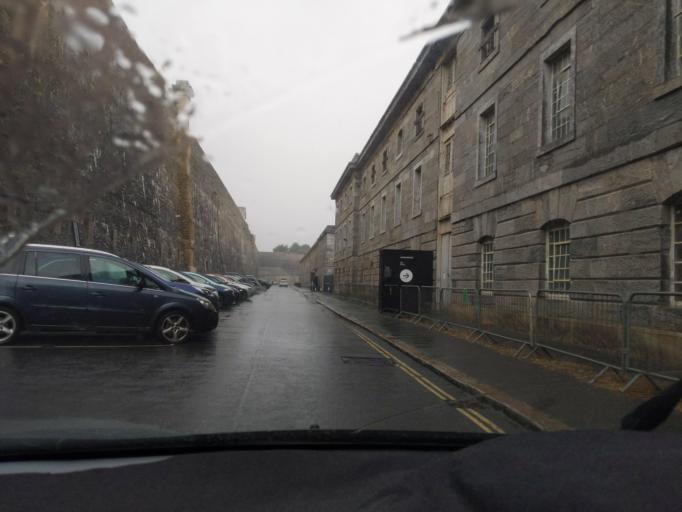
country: GB
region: England
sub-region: Cornwall
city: Millbrook
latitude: 50.3612
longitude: -4.1640
